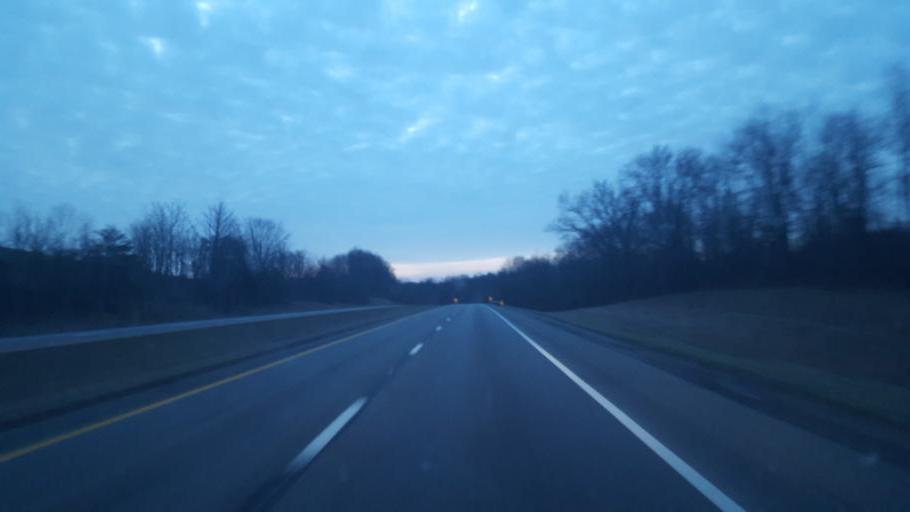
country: US
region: Ohio
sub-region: Jackson County
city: Oak Hill
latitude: 38.9804
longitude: -82.5257
